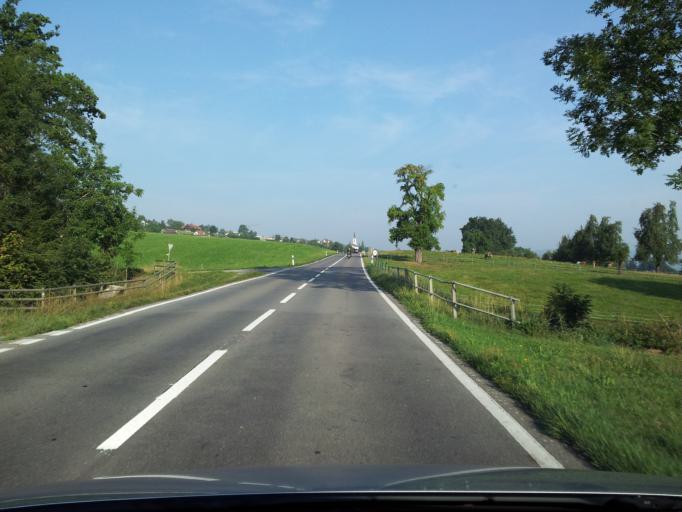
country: CH
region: Lucerne
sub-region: Sursee District
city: Nottwil
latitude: 47.1254
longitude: 8.1568
